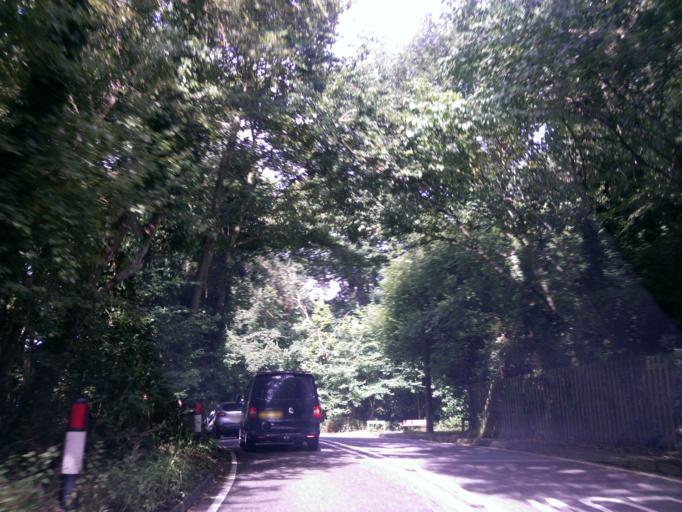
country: GB
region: England
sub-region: Essex
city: Sible Hedingham
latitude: 51.9516
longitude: 0.6354
